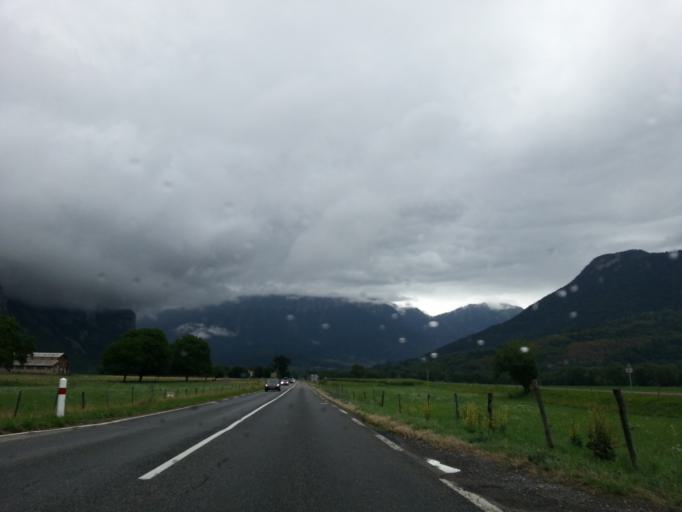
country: FR
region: Rhone-Alpes
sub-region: Departement de la Haute-Savoie
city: Doussard
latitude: 45.7651
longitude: 6.2501
